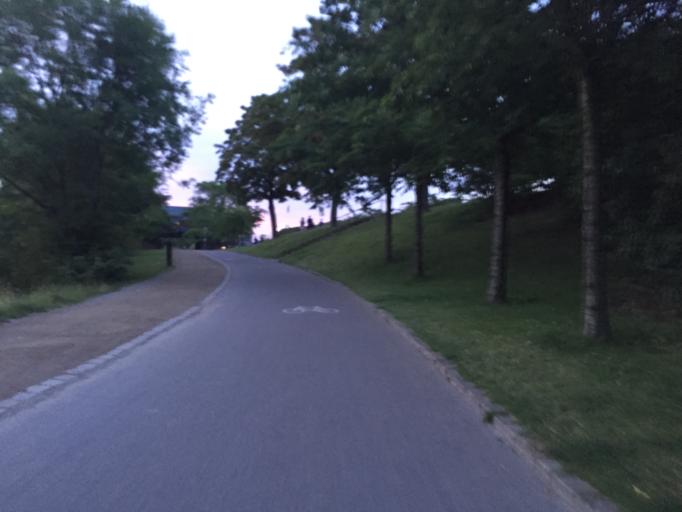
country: DK
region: Capital Region
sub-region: Kobenhavn
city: Christianshavn
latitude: 55.6902
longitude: 12.5985
